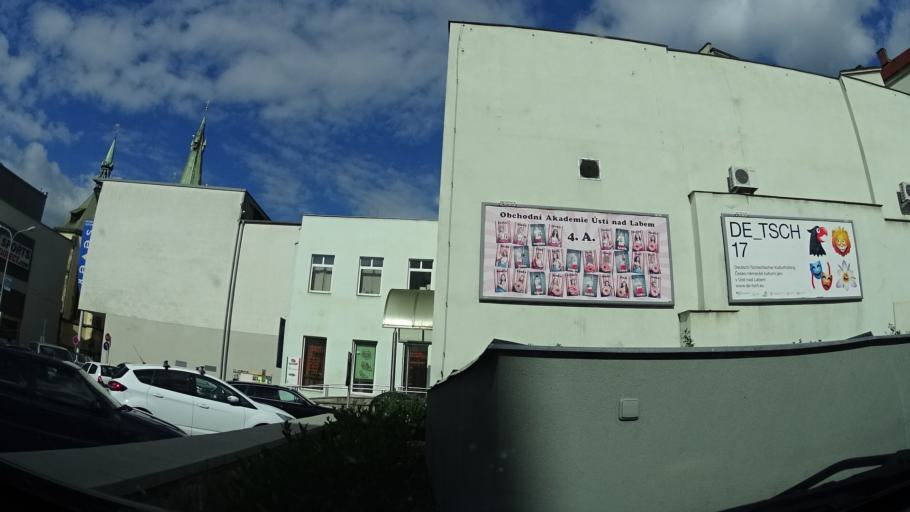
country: CZ
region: Ustecky
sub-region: Okres Usti nad Labem
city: Usti nad Labem
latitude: 50.6596
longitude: 14.0417
